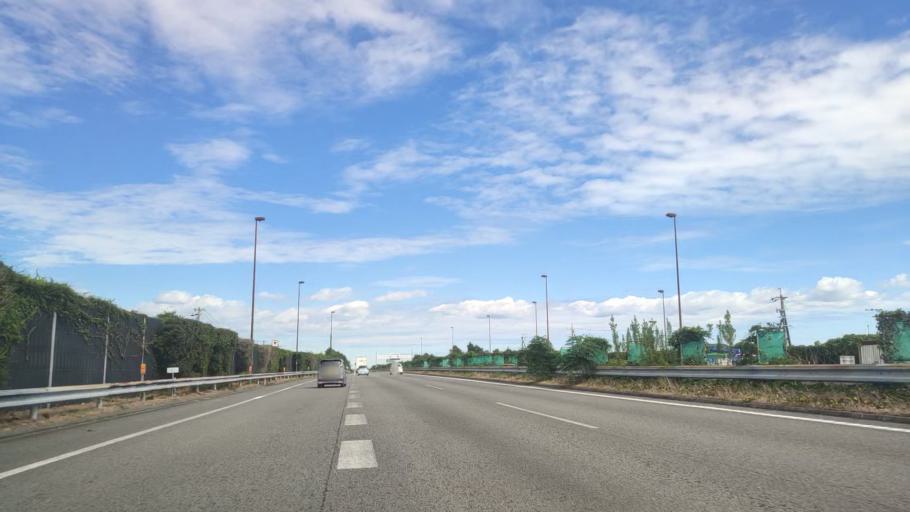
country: JP
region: Shizuoka
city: Hamamatsu
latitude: 34.7652
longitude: 137.6796
